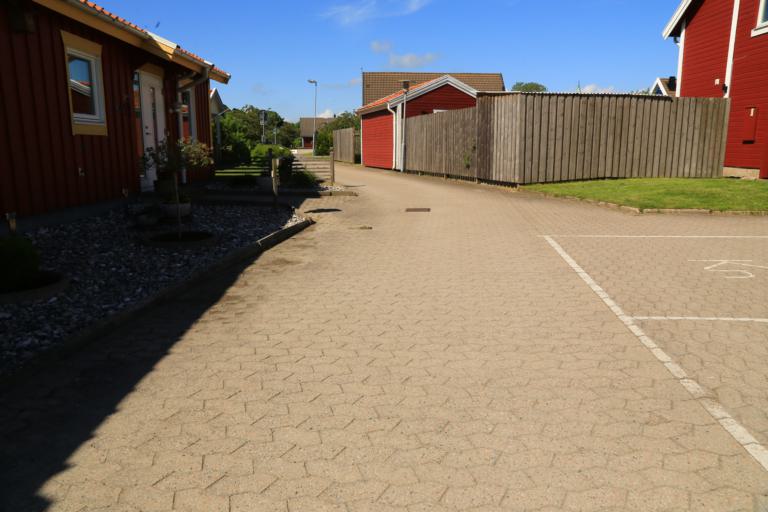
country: SE
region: Halland
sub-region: Varbergs Kommun
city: Traslovslage
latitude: 57.1048
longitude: 12.2958
